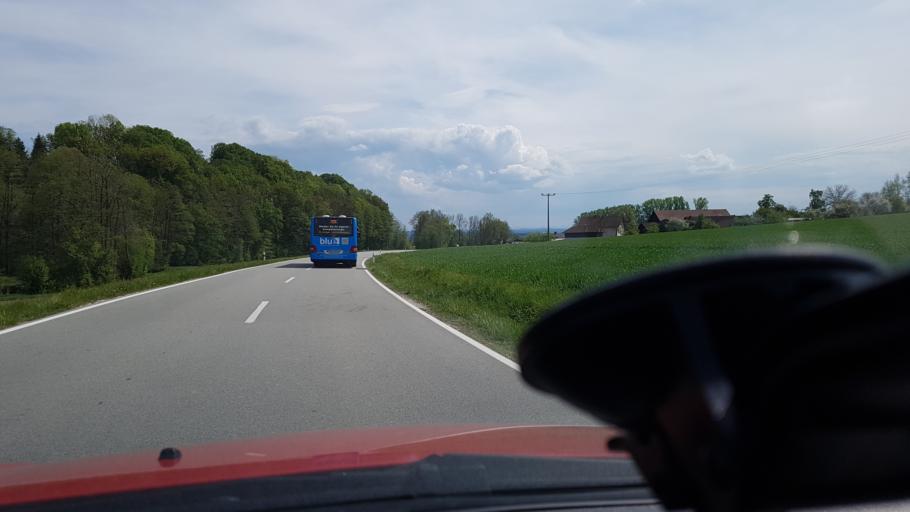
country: DE
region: Bavaria
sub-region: Lower Bavaria
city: Ering
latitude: 48.3188
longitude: 13.1357
